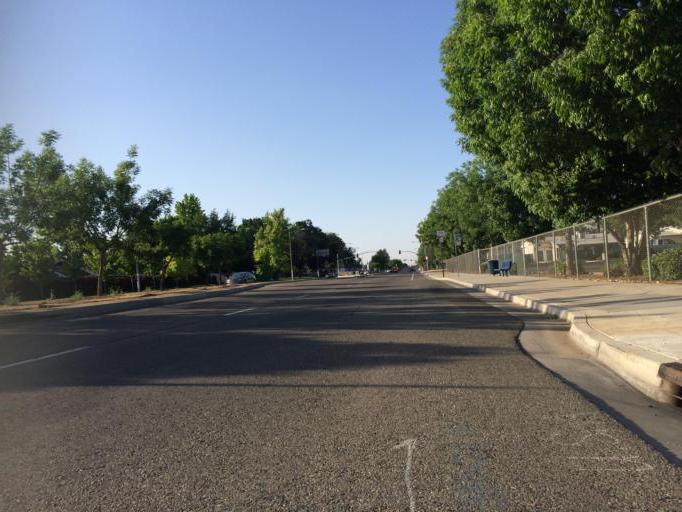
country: US
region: California
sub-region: Fresno County
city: Sunnyside
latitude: 36.7542
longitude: -119.7181
